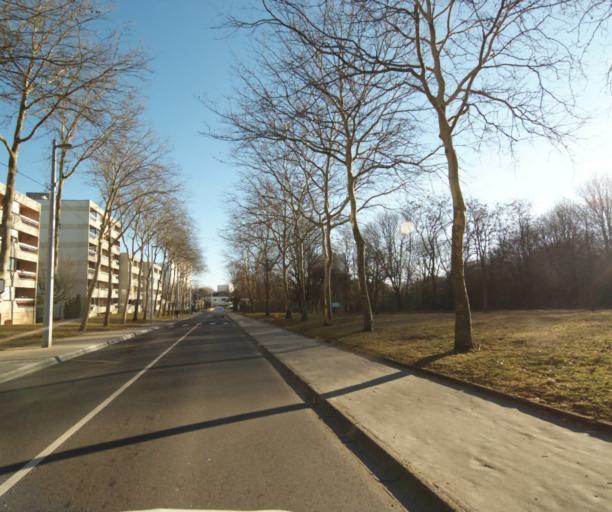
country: FR
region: Lorraine
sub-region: Departement de Meurthe-et-Moselle
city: Laxou
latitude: 48.6991
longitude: 6.1279
